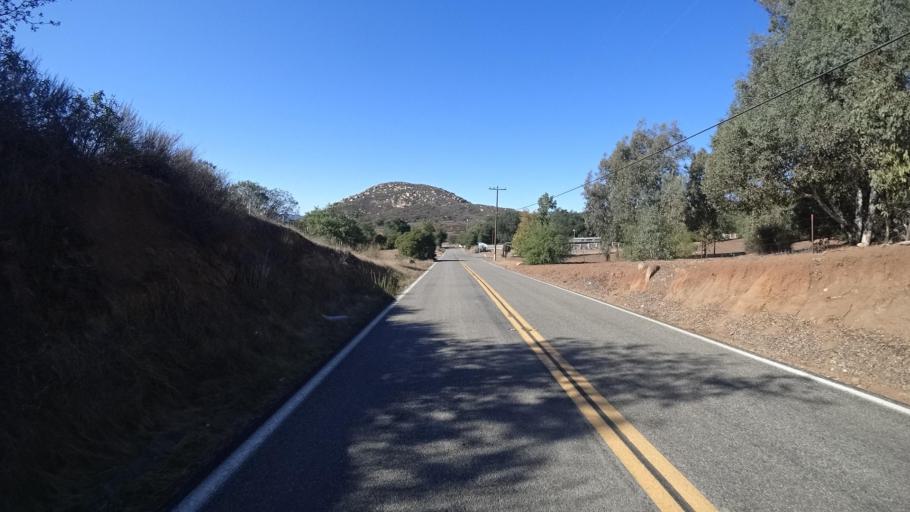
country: US
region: California
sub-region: San Diego County
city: Jamul
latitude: 32.6852
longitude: -116.7524
